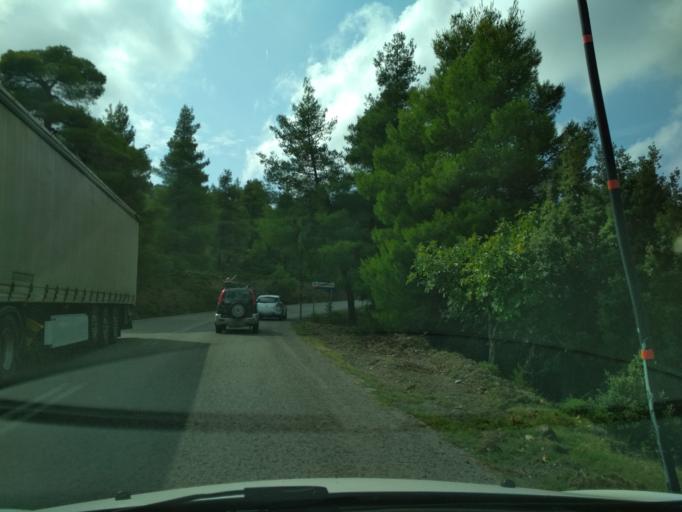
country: GR
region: Central Greece
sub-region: Nomos Evvoias
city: Politika
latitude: 38.6734
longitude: 23.5573
